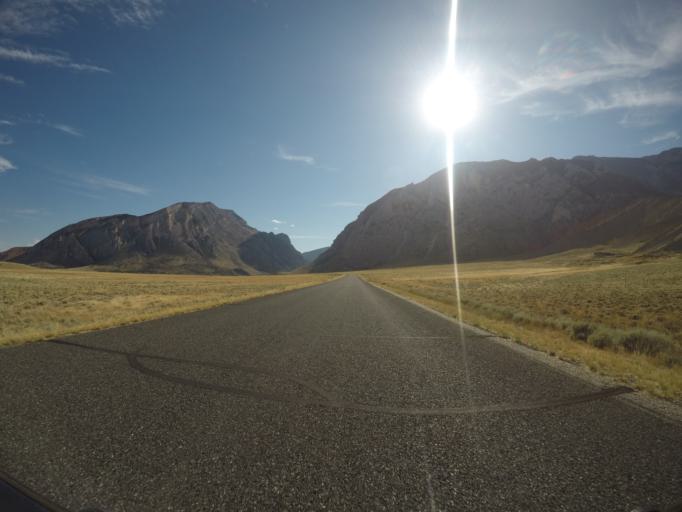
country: US
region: Montana
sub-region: Carbon County
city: Red Lodge
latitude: 44.8642
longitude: -109.2833
